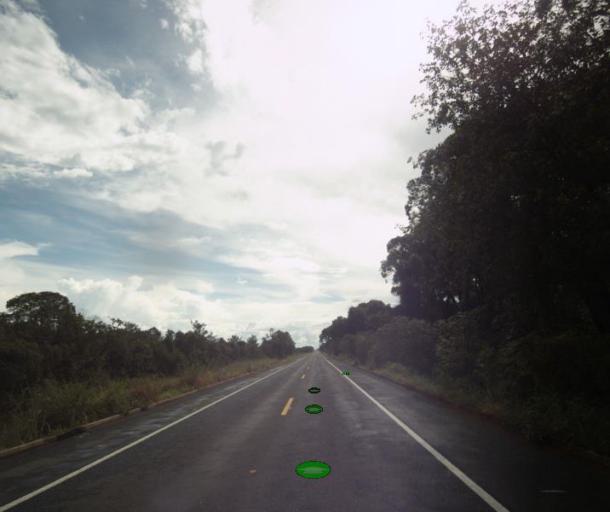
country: BR
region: Goias
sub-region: Sao Miguel Do Araguaia
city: Sao Miguel do Araguaia
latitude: -13.2863
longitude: -50.4745
